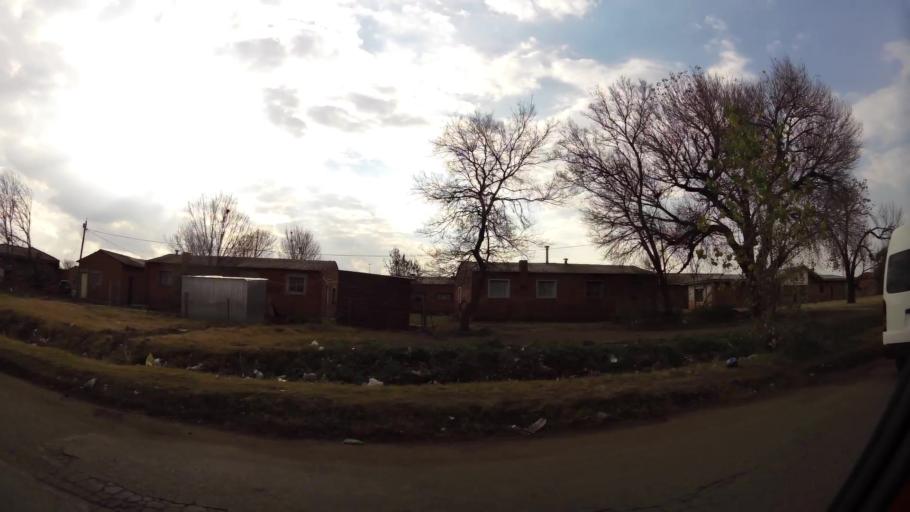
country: ZA
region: Gauteng
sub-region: Sedibeng District Municipality
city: Vereeniging
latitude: -26.6778
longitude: 27.8893
